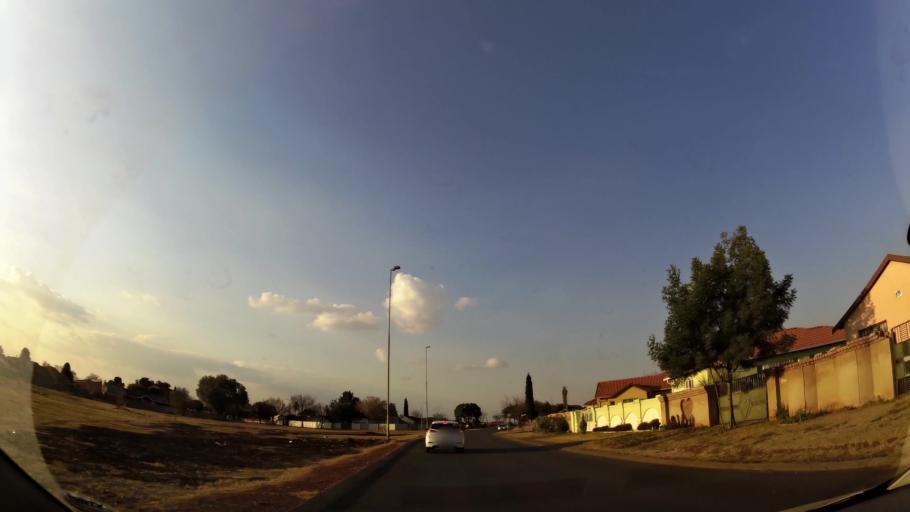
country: ZA
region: Gauteng
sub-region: Ekurhuleni Metropolitan Municipality
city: Boksburg
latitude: -26.2981
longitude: 28.2490
